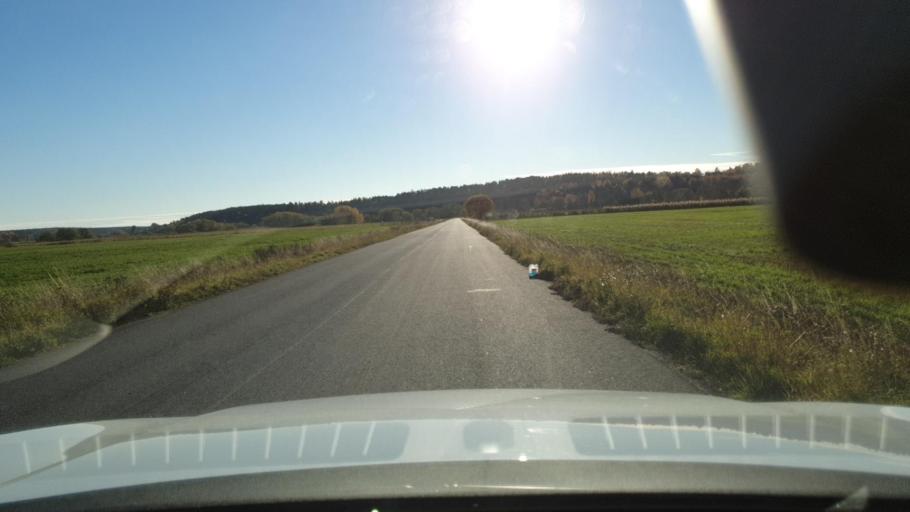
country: SE
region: Uppsala
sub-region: Uppsala Kommun
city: Uppsala
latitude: 59.8392
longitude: 17.6687
